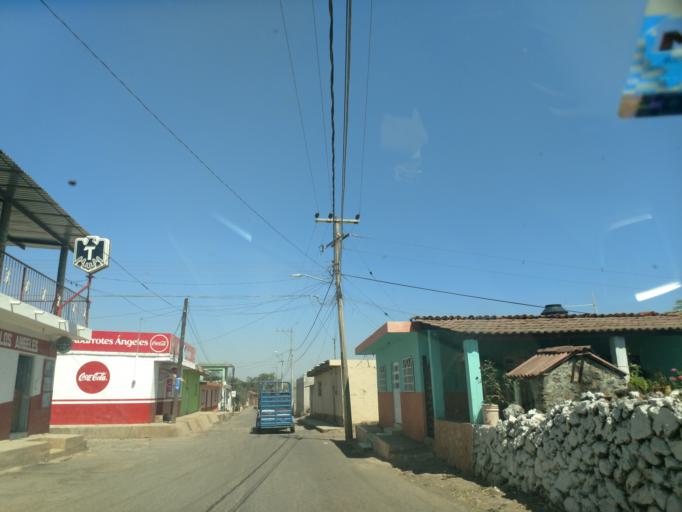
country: MX
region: Nayarit
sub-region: Tepic
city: La Corregidora
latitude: 21.5042
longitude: -104.7089
